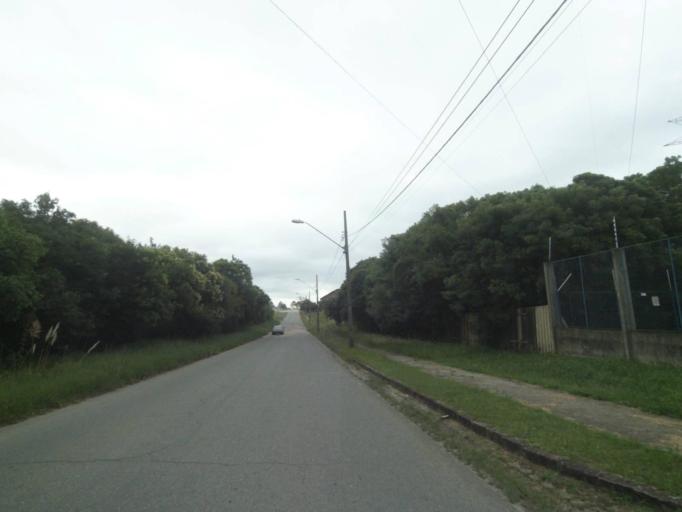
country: BR
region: Parana
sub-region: Sao Jose Dos Pinhais
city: Sao Jose dos Pinhais
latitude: -25.5447
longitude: -49.3129
